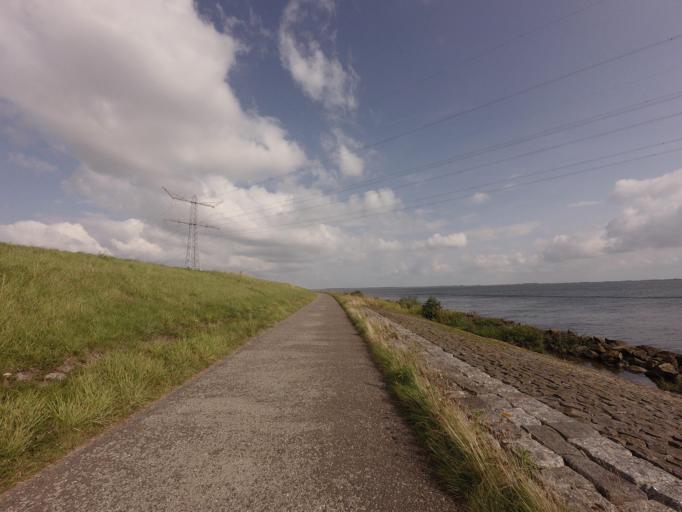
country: NL
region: Flevoland
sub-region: Gemeente Urk
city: Urk
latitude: 52.6133
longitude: 5.6610
